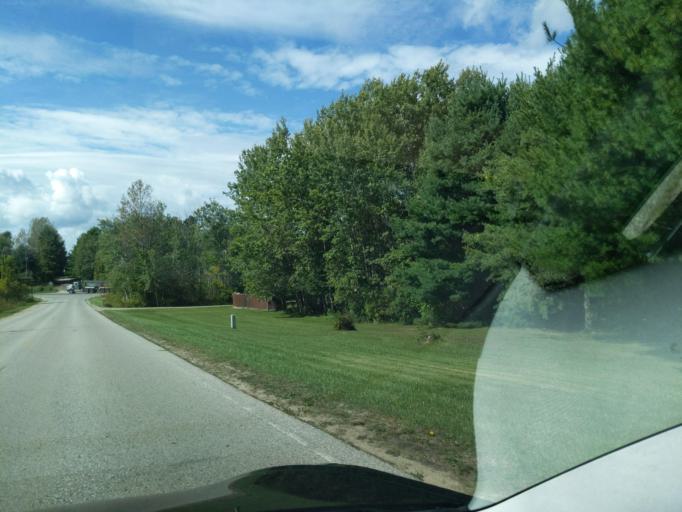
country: US
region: Michigan
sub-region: Antrim County
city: Bellaire
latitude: 45.0347
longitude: -85.3498
